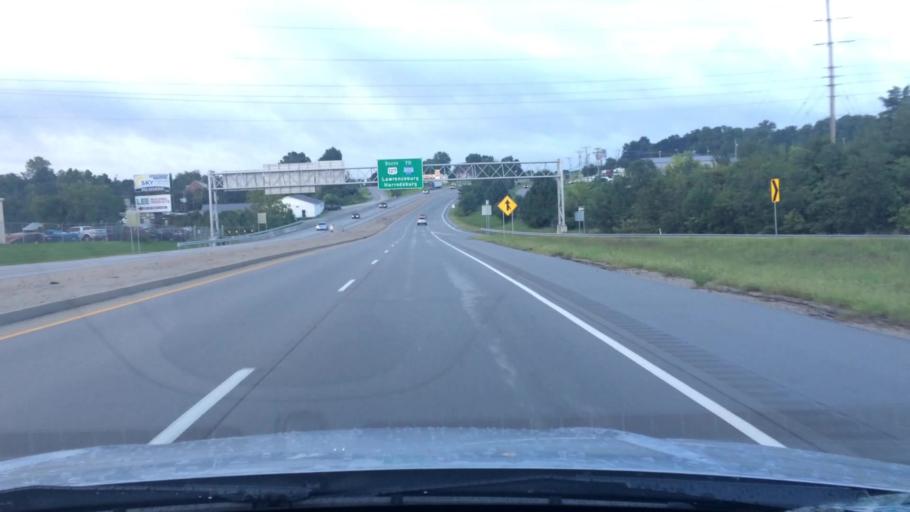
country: US
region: Kentucky
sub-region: Franklin County
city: Frankfort
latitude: 38.1559
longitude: -84.8941
